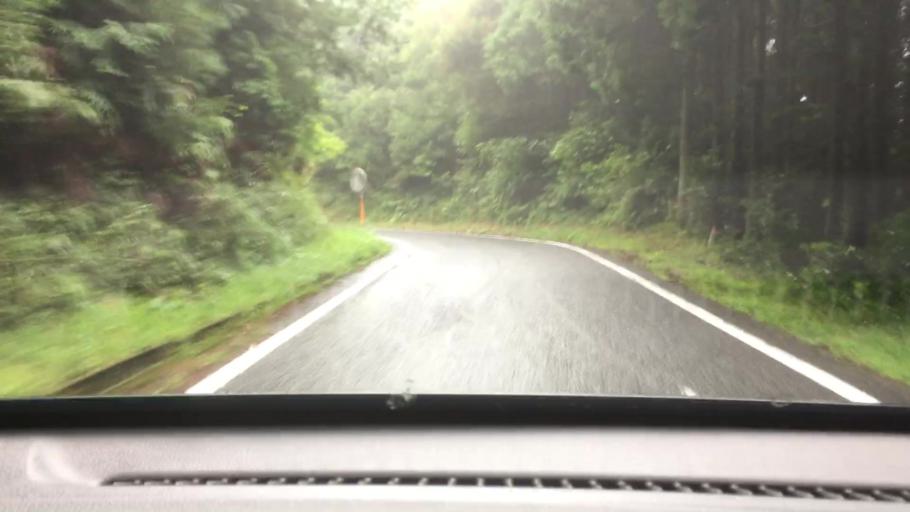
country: JP
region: Nagasaki
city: Togitsu
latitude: 32.9166
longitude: 129.7303
